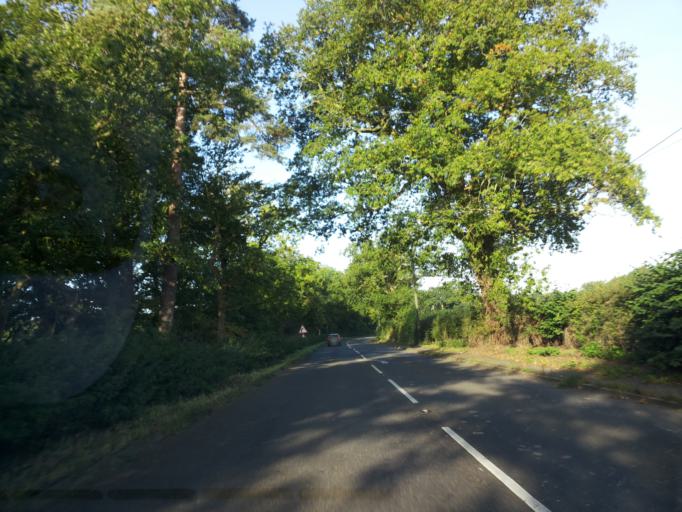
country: GB
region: England
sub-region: Warwickshire
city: Wroxall
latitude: 52.3401
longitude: -1.6779
